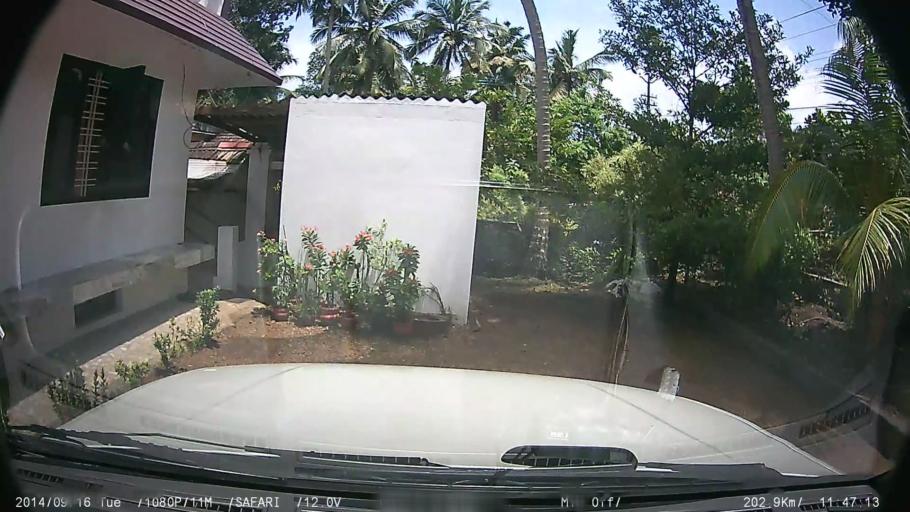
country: IN
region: Kerala
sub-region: Kottayam
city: Changanacheri
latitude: 9.4274
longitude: 76.5611
